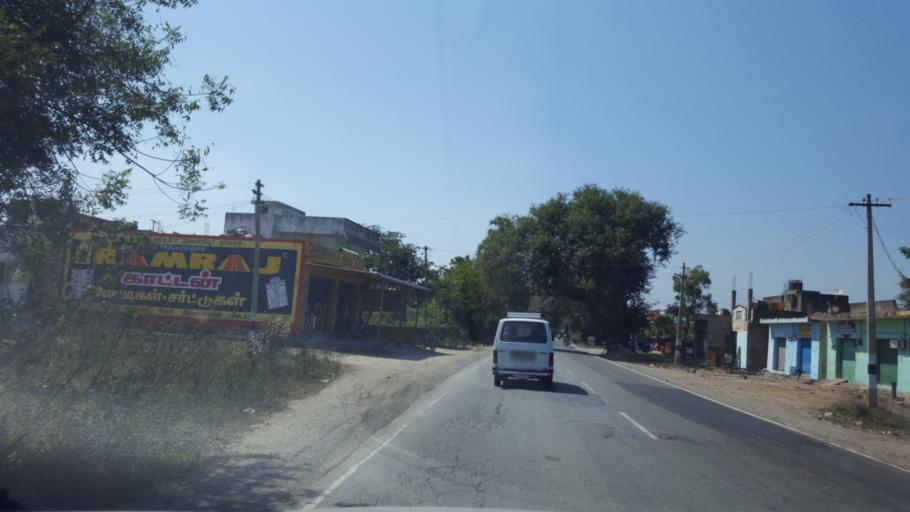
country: IN
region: Tamil Nadu
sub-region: Kancheepuram
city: Wallajahbad
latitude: 12.7804
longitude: 79.8497
